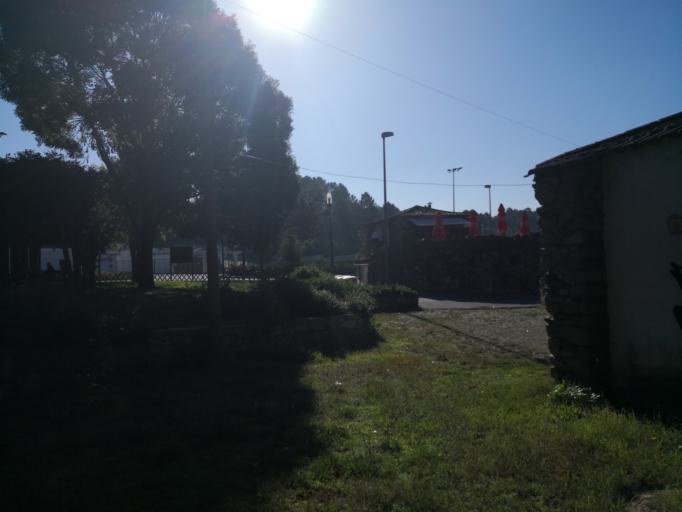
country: PT
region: Vila Real
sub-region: Vila Real
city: Vila Real
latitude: 41.3053
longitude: -7.7355
